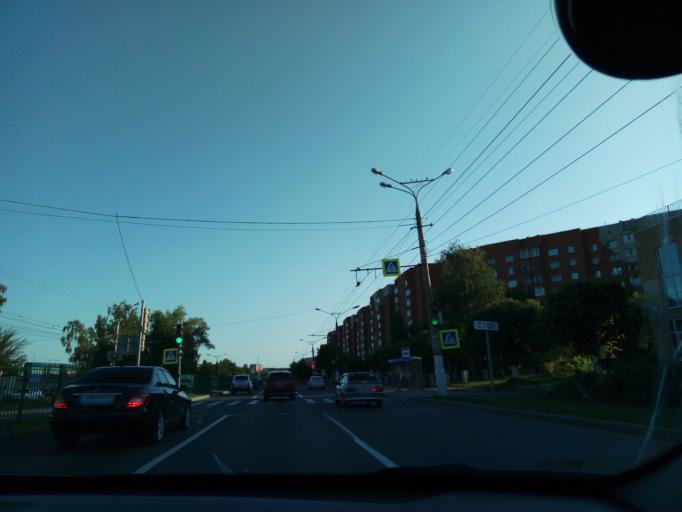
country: RU
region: Chuvashia
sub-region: Cheboksarskiy Rayon
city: Cheboksary
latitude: 56.1161
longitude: 47.2738
